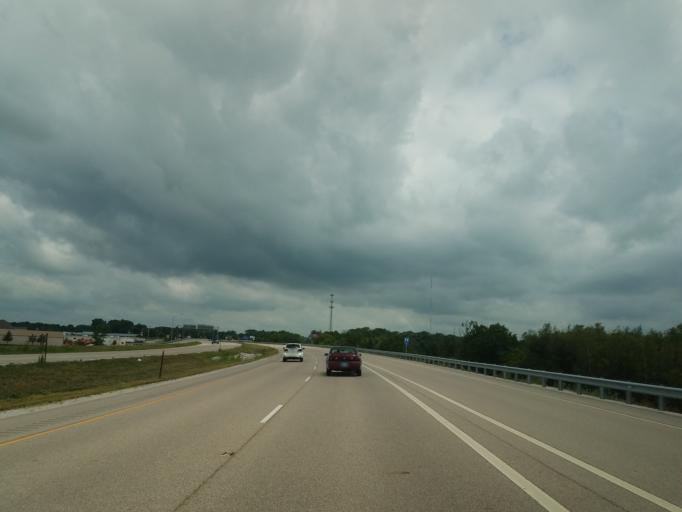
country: US
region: Illinois
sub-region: McLean County
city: Bloomington
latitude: 40.4434
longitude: -89.0167
